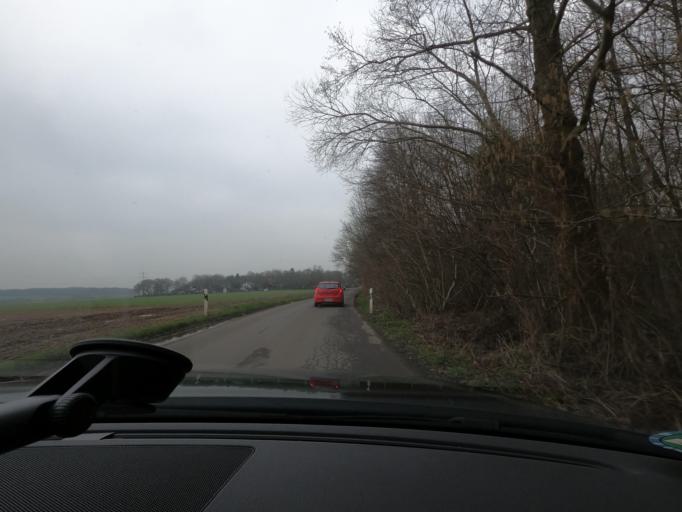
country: DE
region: North Rhine-Westphalia
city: Tonisvorst
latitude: 51.3915
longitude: 6.5173
